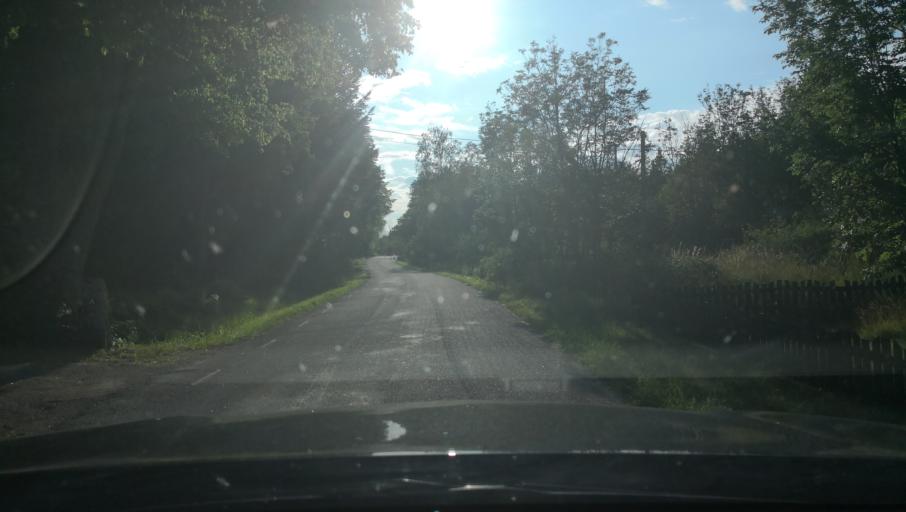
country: SE
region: Uppsala
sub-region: Osthammars Kommun
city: Osterbybruk
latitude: 60.0203
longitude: 17.9591
